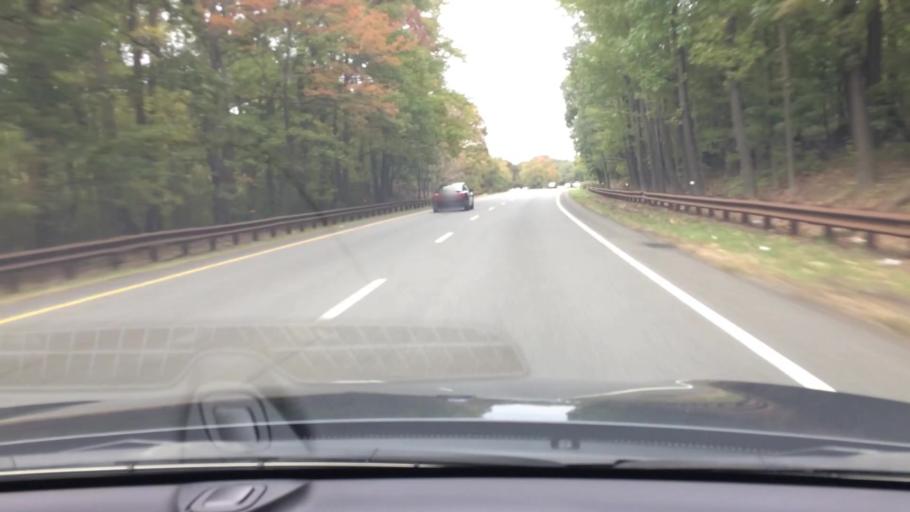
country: US
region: New Jersey
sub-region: Bergen County
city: Englewood Cliffs
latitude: 40.9030
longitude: -73.9361
